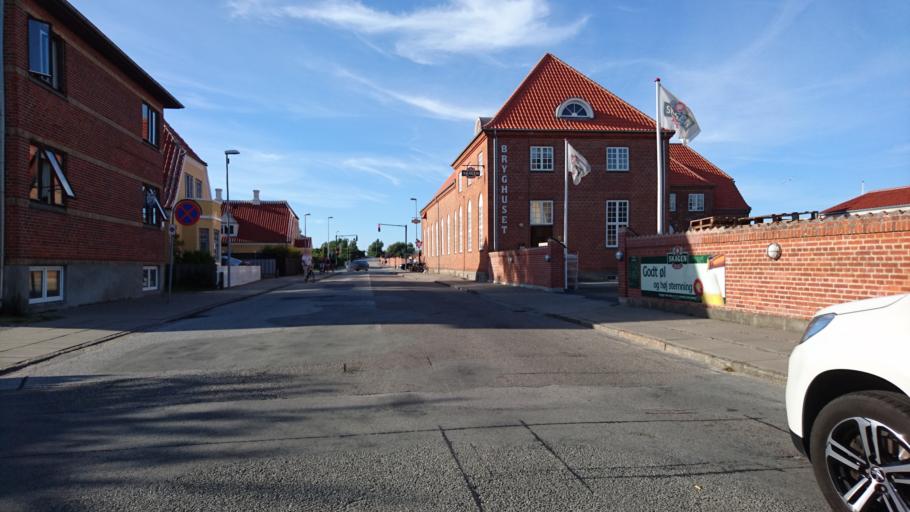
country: DK
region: North Denmark
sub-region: Frederikshavn Kommune
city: Skagen
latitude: 57.7219
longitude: 10.5836
